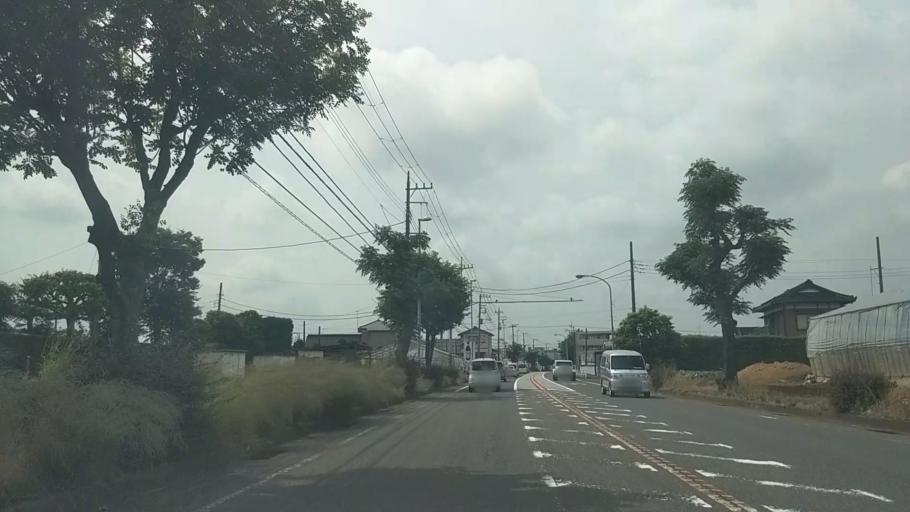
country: JP
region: Kanagawa
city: Fujisawa
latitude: 35.3727
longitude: 139.4786
